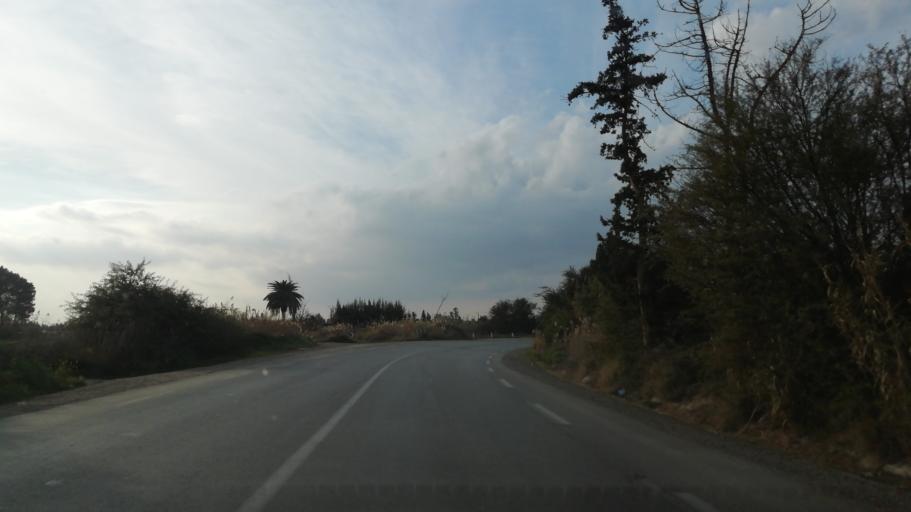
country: DZ
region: Mascara
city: Mascara
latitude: 35.6174
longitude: 0.0493
